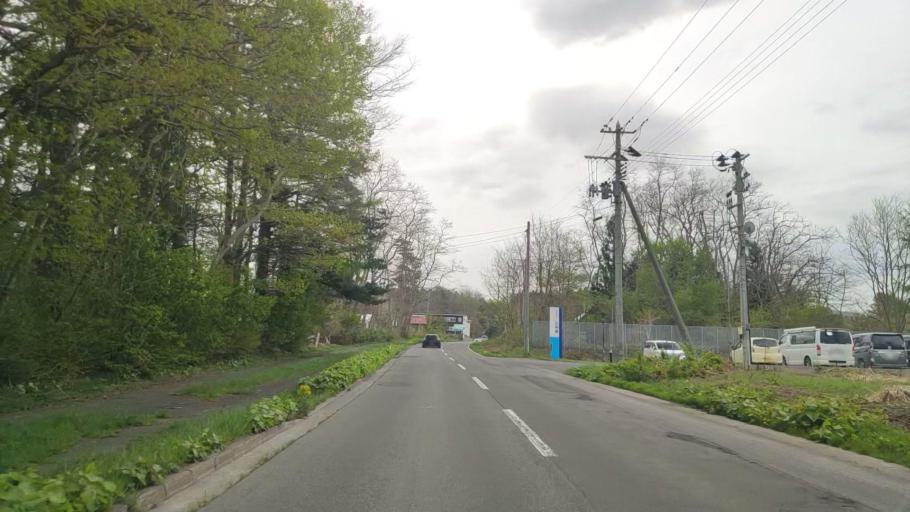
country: JP
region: Aomori
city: Aomori Shi
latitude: 40.7677
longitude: 140.8007
